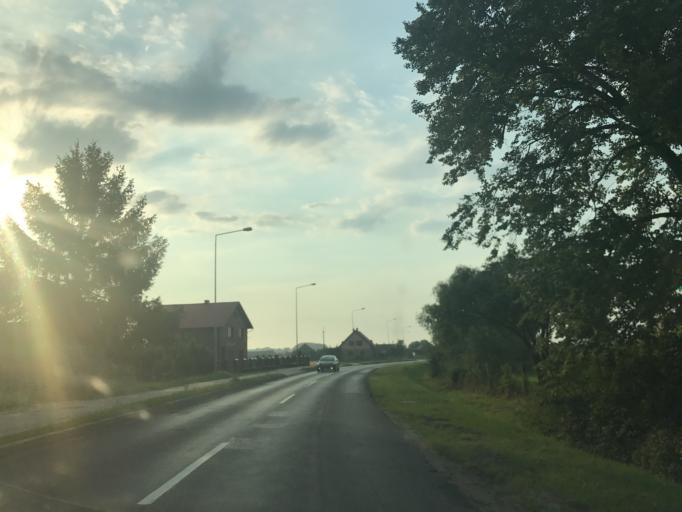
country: PL
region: Greater Poland Voivodeship
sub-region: Powiat rawicki
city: Rawicz
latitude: 51.6073
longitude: 16.8843
